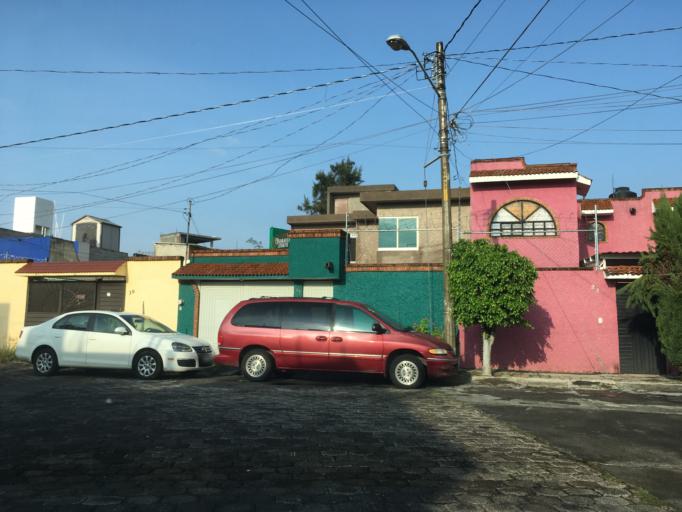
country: MX
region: Michoacan
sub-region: Morelia
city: Morelos
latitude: 19.6835
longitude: -101.2252
